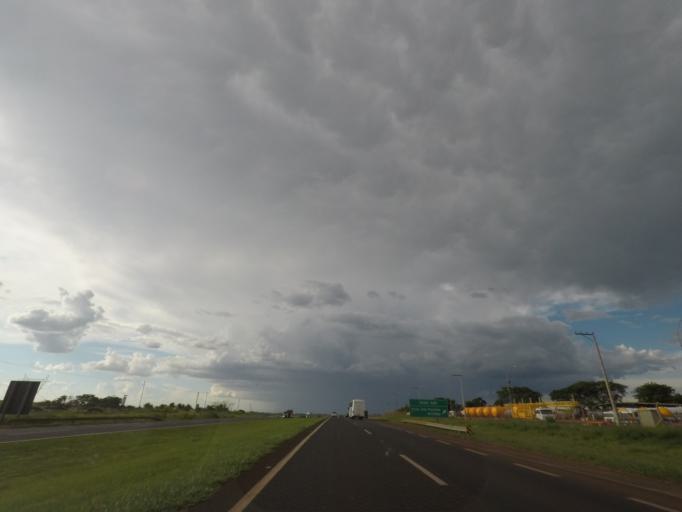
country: BR
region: Sao Paulo
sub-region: Jardinopolis
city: Jardinopolis
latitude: -21.0370
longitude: -47.8319
